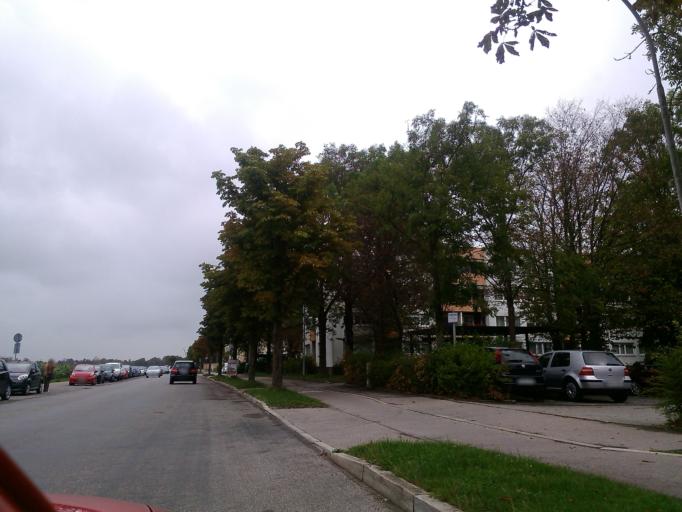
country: DE
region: Bavaria
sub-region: Upper Bavaria
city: Fuerstenfeldbruck
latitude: 48.1799
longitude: 11.2374
